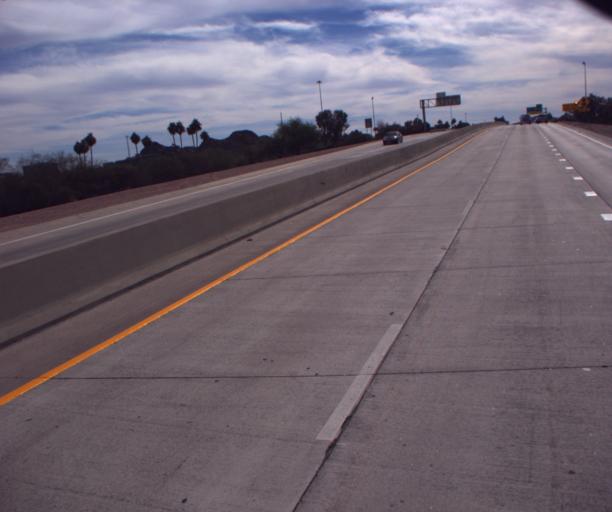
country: US
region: Arizona
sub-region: Maricopa County
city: Tempe Junction
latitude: 33.4129
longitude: -111.9783
